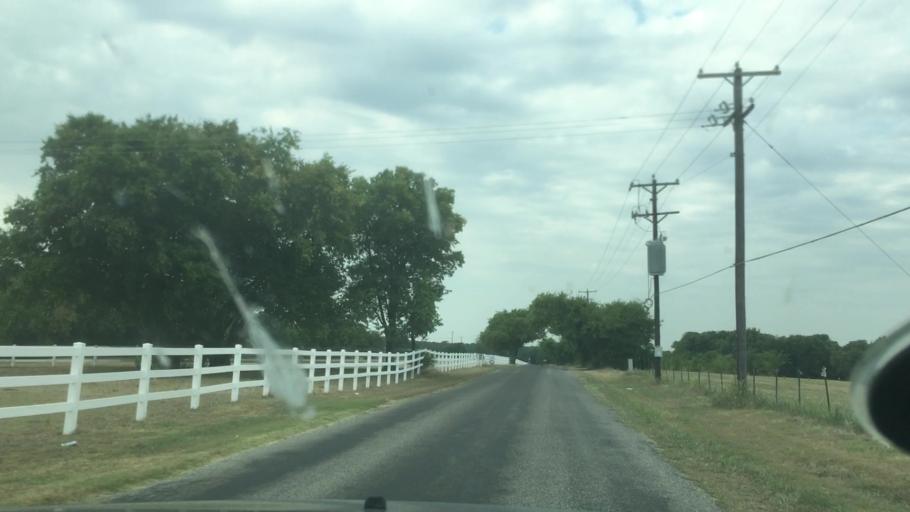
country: US
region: Texas
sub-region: Grayson County
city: Pottsboro
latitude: 33.8094
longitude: -96.7032
